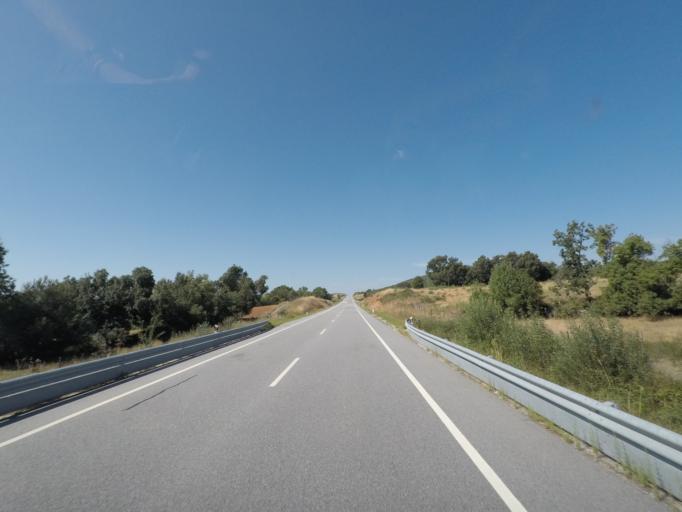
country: PT
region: Braganca
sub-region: Mogadouro
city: Mogadouro
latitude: 41.3524
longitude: -6.5943
